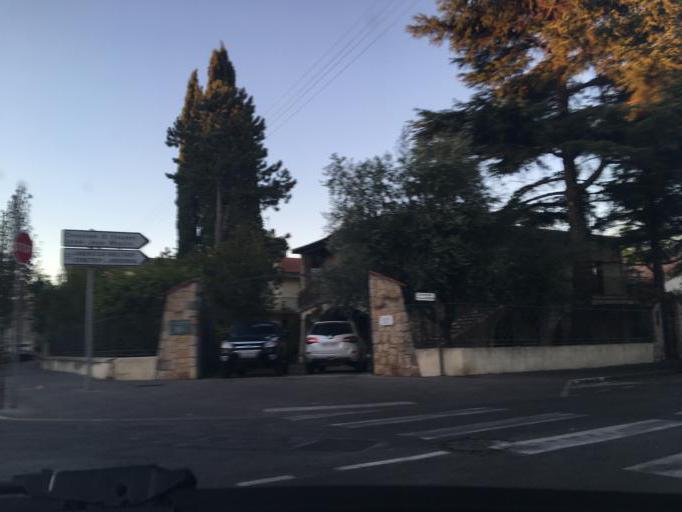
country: FR
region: Provence-Alpes-Cote d'Azur
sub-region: Departement du Var
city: Draguignan
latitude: 43.5334
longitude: 6.4699
